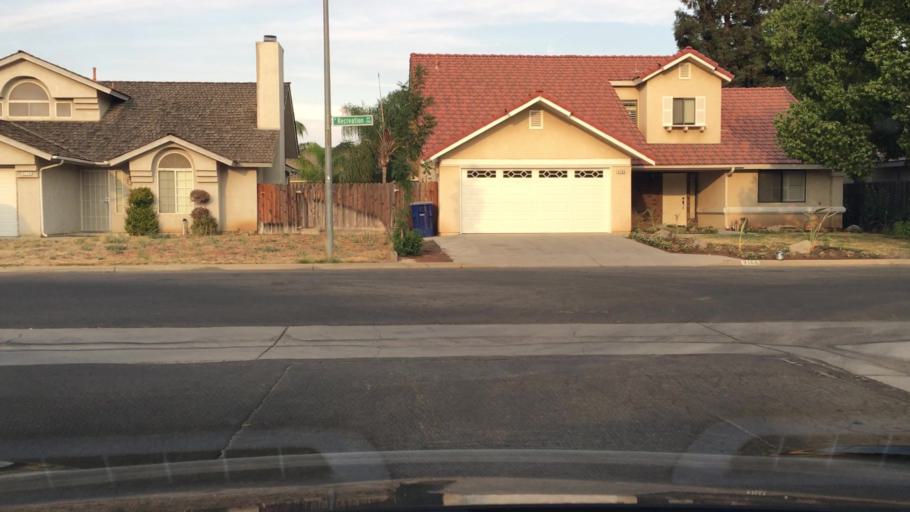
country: US
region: California
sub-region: Fresno County
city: Clovis
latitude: 36.8694
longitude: -119.7425
